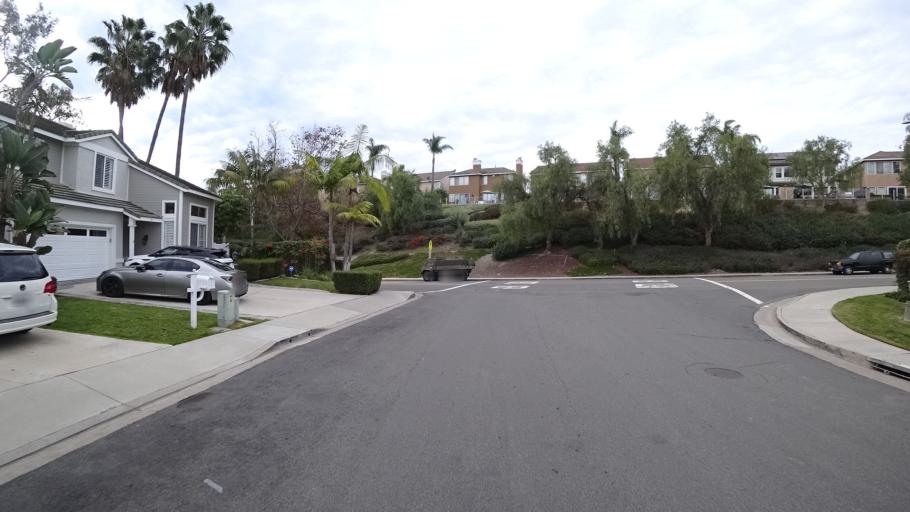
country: US
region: California
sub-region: Orange County
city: Aliso Viejo
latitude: 33.5766
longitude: -117.7371
